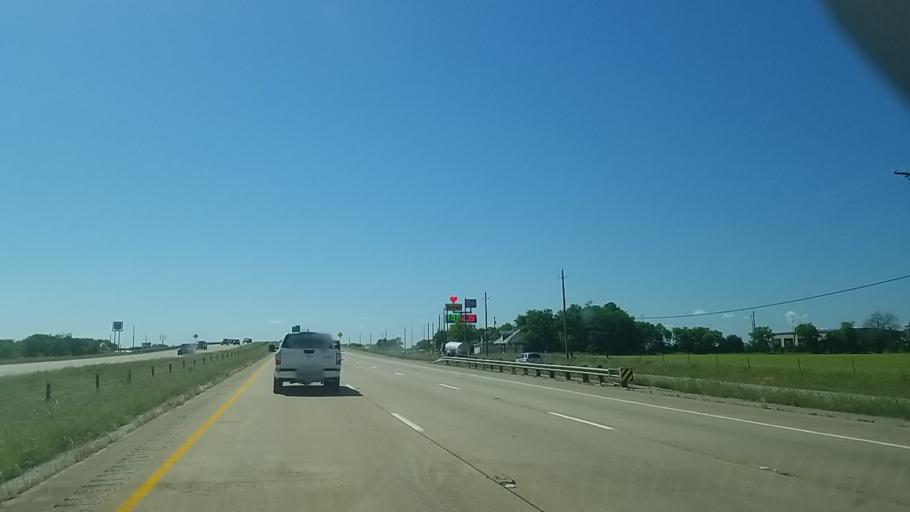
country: US
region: Texas
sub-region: Ellis County
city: Ennis
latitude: 32.2849
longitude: -96.5411
